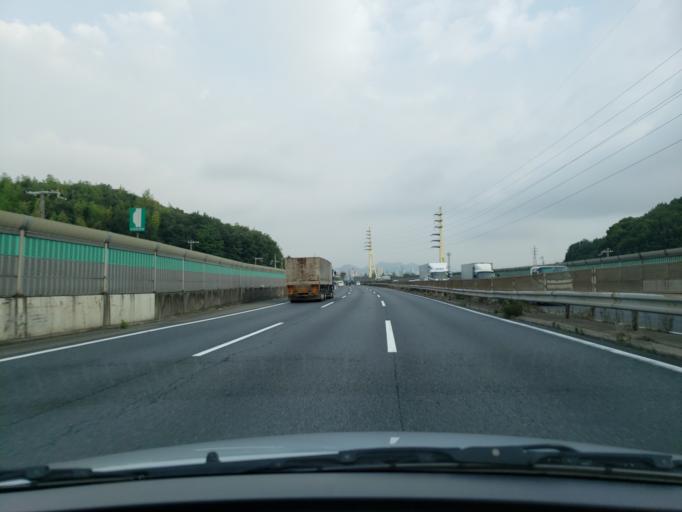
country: JP
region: Hyogo
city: Himeji
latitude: 34.8044
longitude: 134.7041
